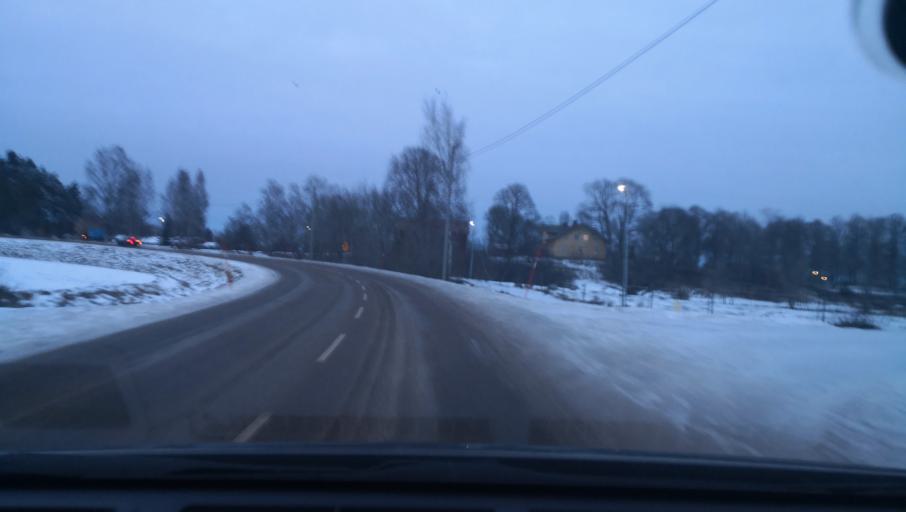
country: SE
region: Dalarna
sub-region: Avesta Kommun
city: Horndal
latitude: 60.2029
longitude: 16.4738
